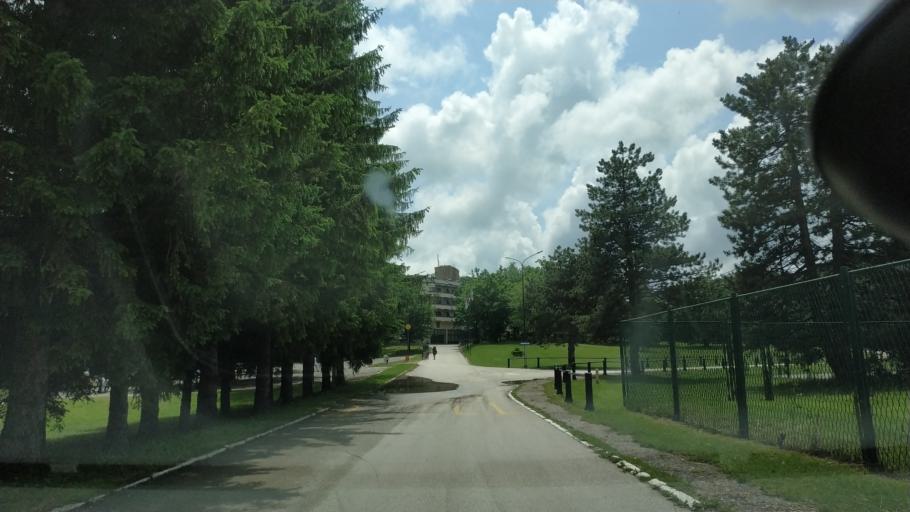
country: RS
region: Central Serbia
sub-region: Borski Okrug
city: Bor
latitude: 44.0907
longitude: 22.0041
